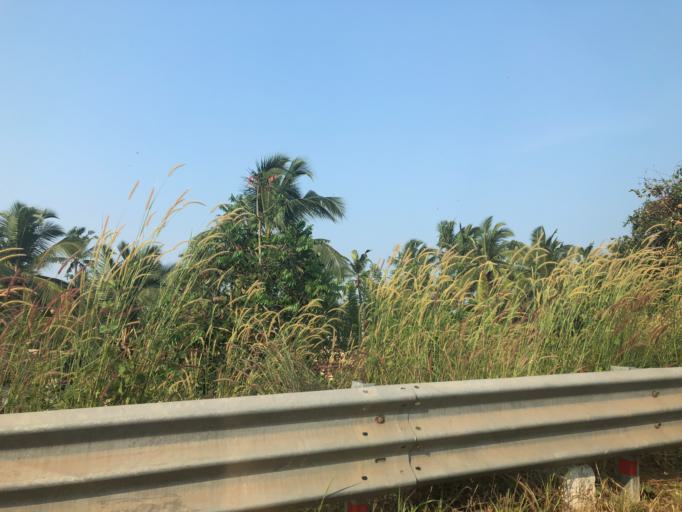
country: IN
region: Karnataka
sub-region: Dakshina Kannada
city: Ullal
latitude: 12.8146
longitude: 74.8558
